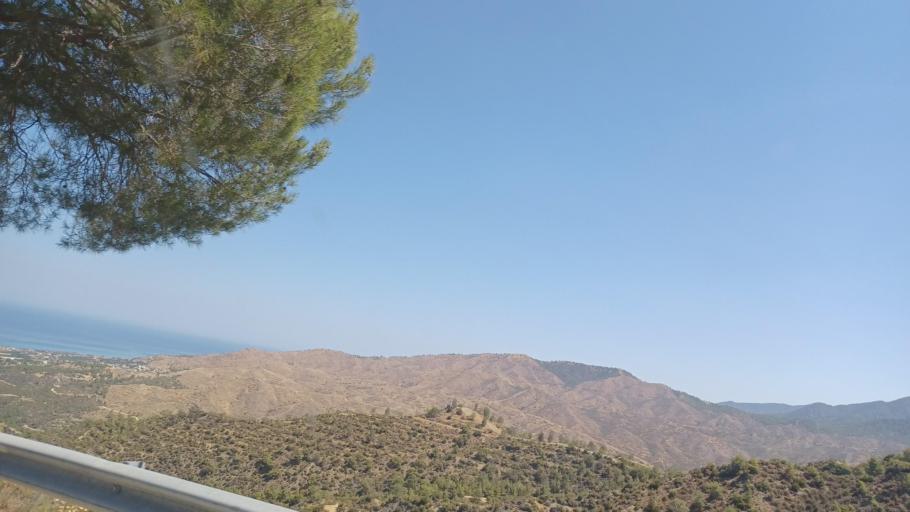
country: CY
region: Pafos
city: Polis
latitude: 35.0371
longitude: 32.5000
